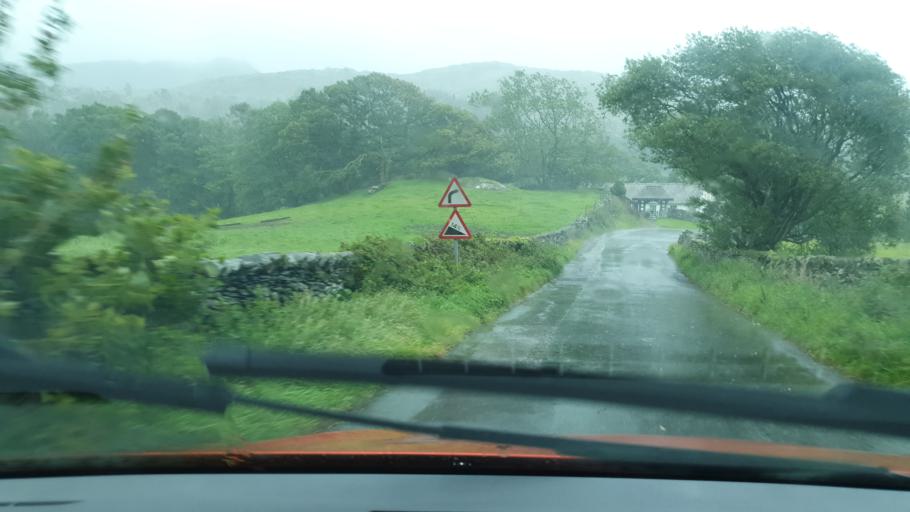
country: GB
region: England
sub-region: Cumbria
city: Millom
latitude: 54.3293
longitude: -3.2358
